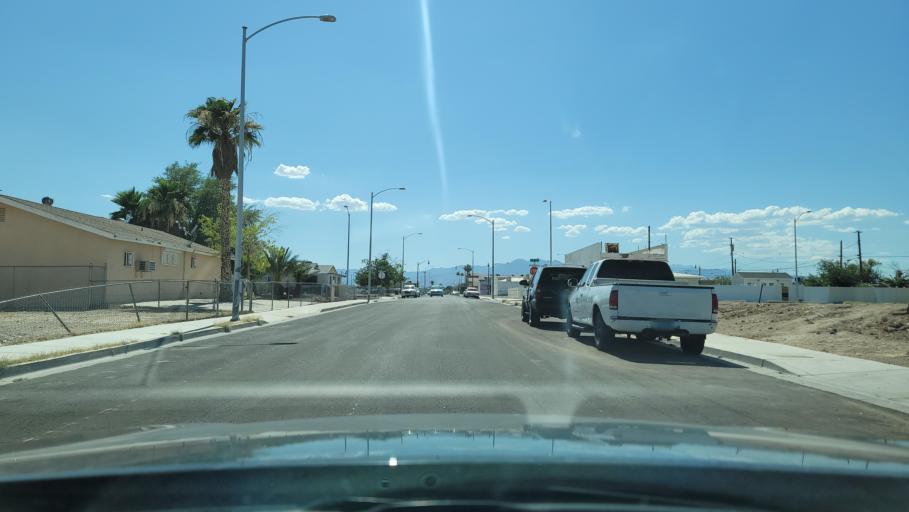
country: US
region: Nevada
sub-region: Clark County
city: Las Vegas
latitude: 36.1850
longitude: -115.1451
